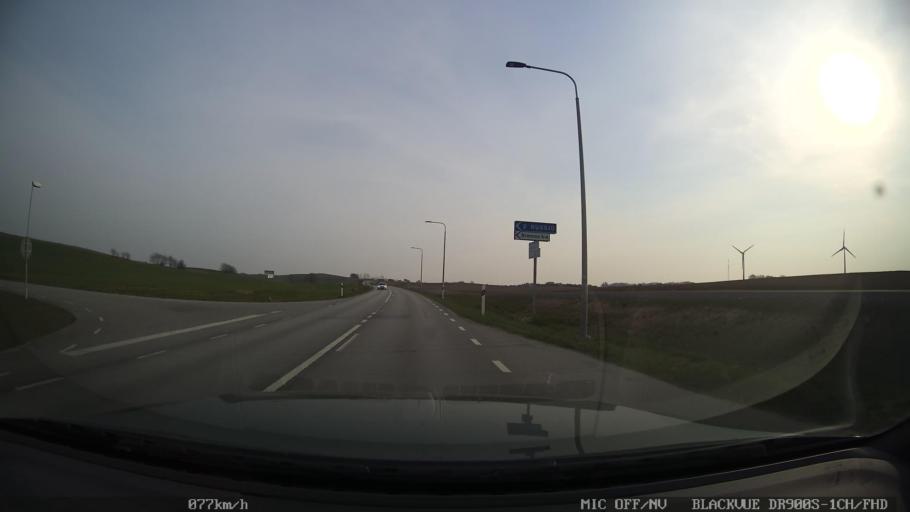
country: SE
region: Skane
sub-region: Ystads Kommun
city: Ystad
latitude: 55.4688
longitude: 13.7970
